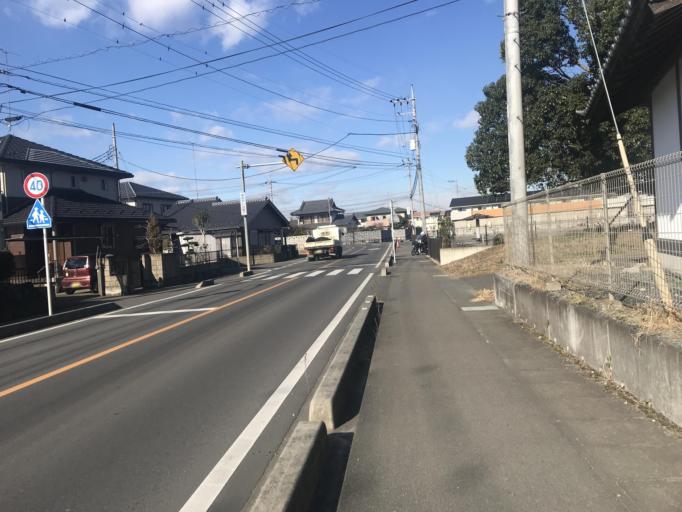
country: JP
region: Tochigi
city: Kaminokawa
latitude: 36.3798
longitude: 139.8769
